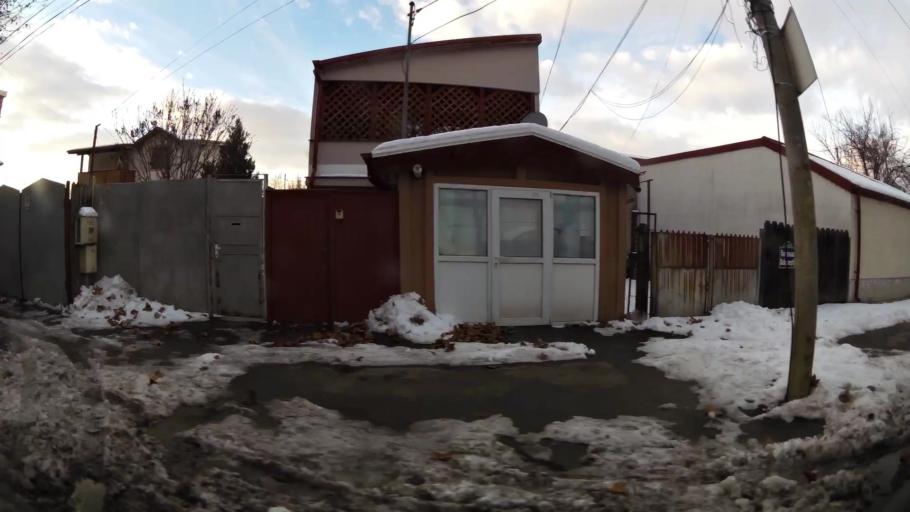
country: RO
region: Ilfov
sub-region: Comuna Fundeni-Dobroesti
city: Fundeni
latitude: 44.4458
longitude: 26.1693
